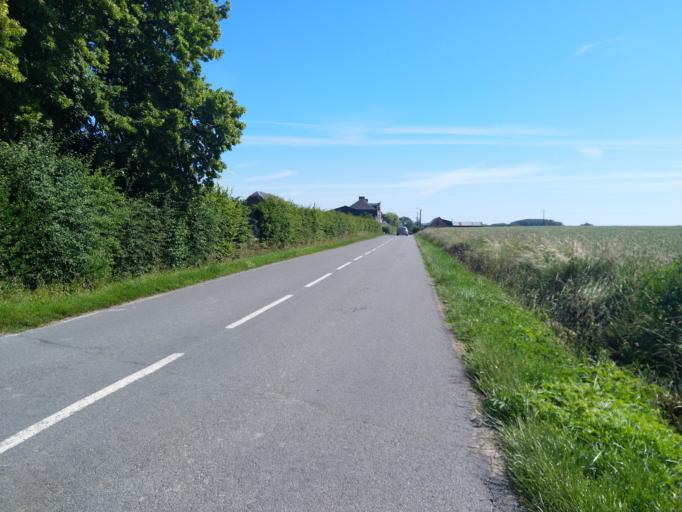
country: FR
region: Nord-Pas-de-Calais
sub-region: Departement du Nord
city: Bavay
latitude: 50.3188
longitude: 3.8183
